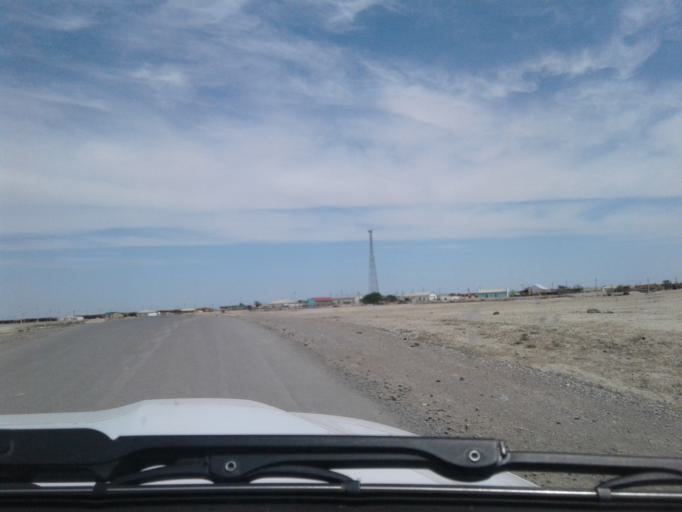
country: TM
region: Balkan
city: Gazanjyk
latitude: 39.2064
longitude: 55.7099
